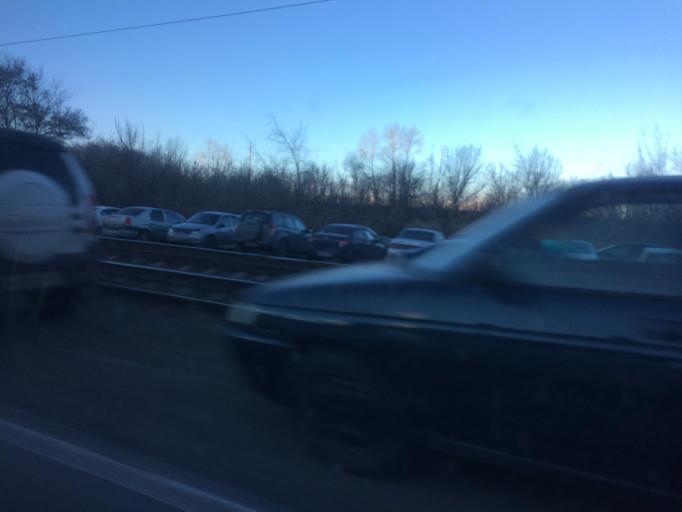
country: RU
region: Chelyabinsk
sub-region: Gorod Magnitogorsk
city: Magnitogorsk
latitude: 53.4015
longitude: 59.0258
